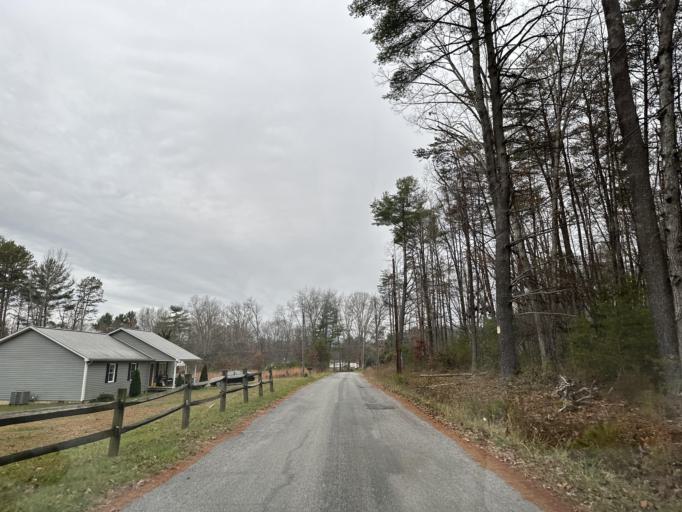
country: US
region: Virginia
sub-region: Rockbridge County
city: East Lexington
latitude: 38.0812
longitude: -79.3890
